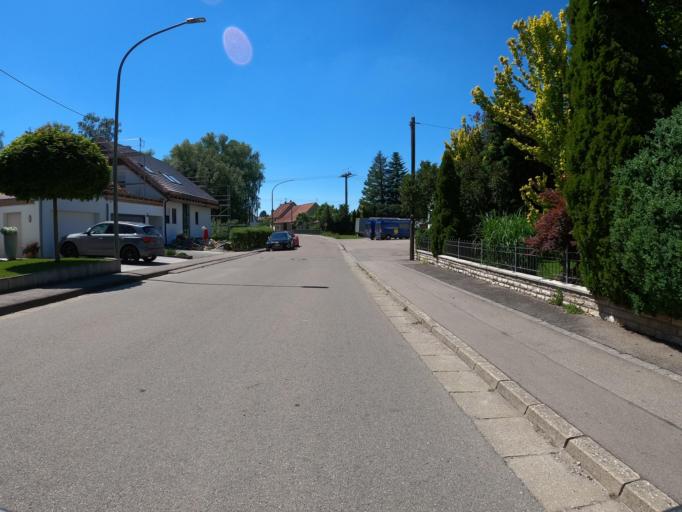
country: DE
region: Bavaria
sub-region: Swabia
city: Pfaffenhofen an der Roth
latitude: 48.3646
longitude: 10.1544
